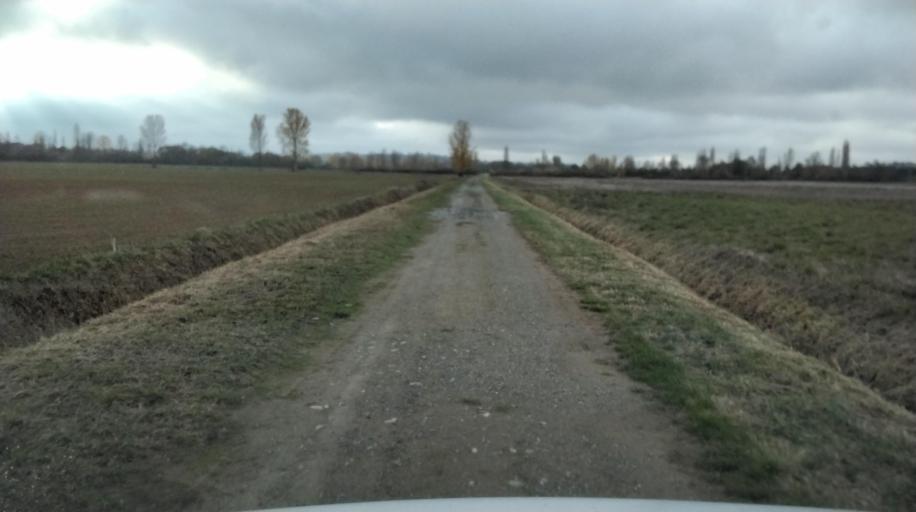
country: FR
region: Midi-Pyrenees
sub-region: Departement de la Haute-Garonne
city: Le Fousseret
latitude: 43.2676
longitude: 1.0339
